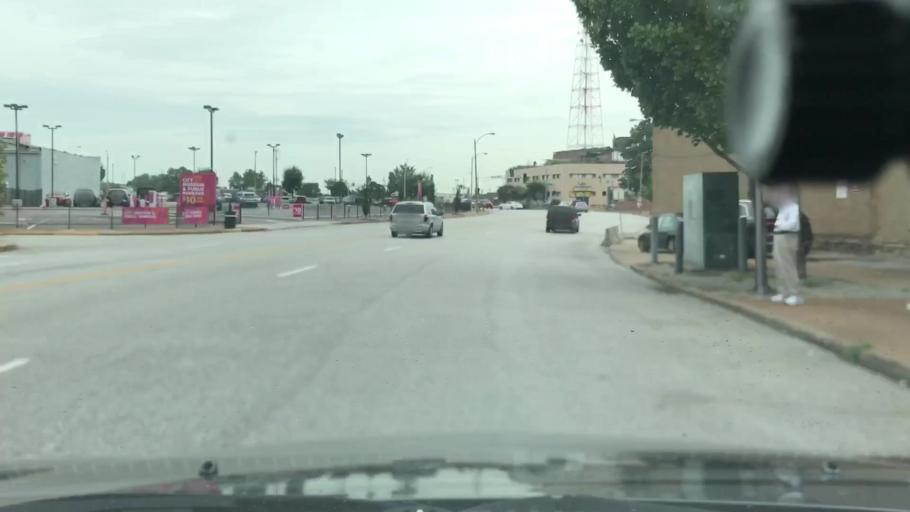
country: US
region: Missouri
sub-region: City of Saint Louis
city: St. Louis
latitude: 38.6326
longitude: -90.1994
